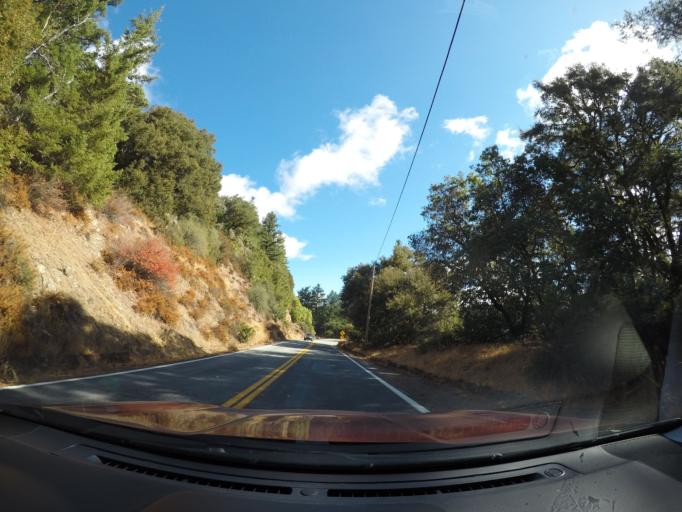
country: US
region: California
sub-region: Santa Clara County
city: Loyola
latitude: 37.2556
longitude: -122.1280
